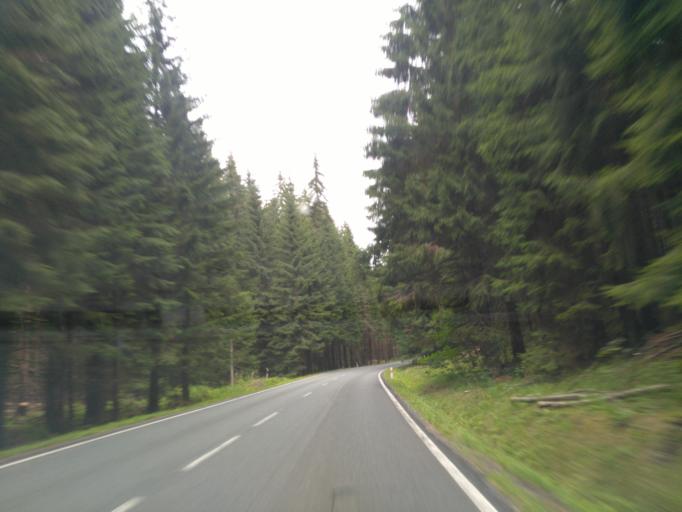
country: DE
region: Saxony
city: Johanngeorgenstadt
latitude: 50.4100
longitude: 12.7360
